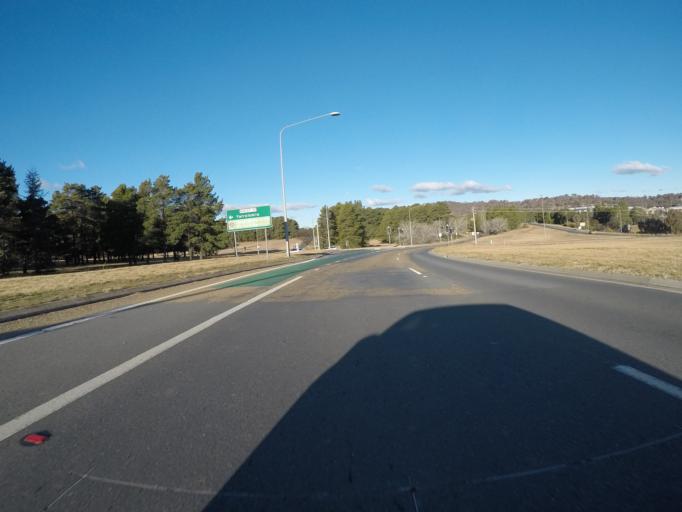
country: AU
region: Australian Capital Territory
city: Forrest
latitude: -35.3125
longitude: 149.0896
